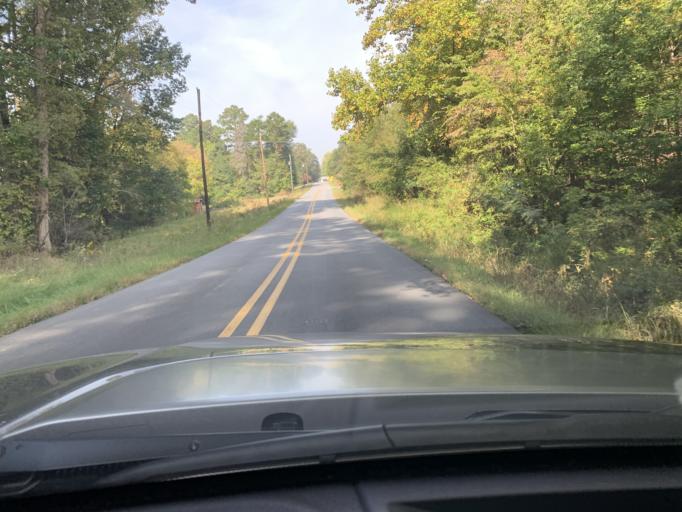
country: US
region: Georgia
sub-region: Polk County
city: Aragon
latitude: 34.0326
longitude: -85.0289
